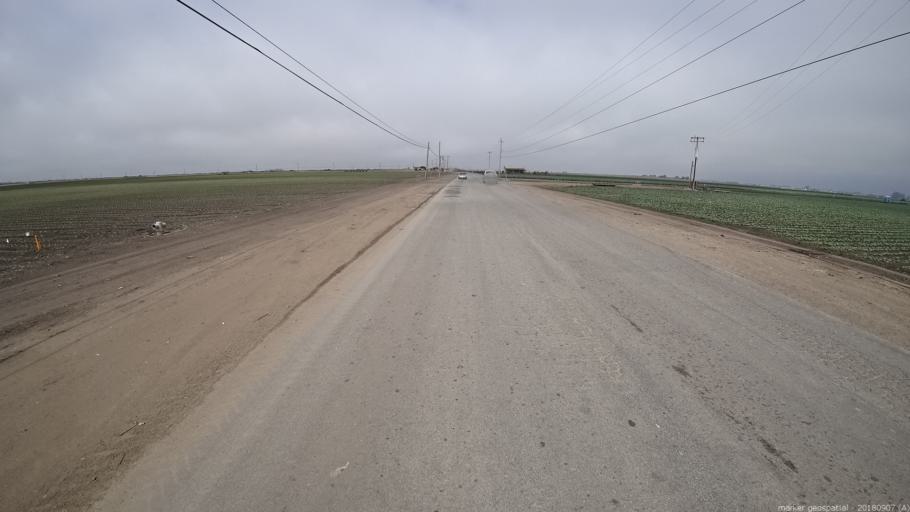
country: US
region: California
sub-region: Monterey County
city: Castroville
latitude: 36.7379
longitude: -121.7623
